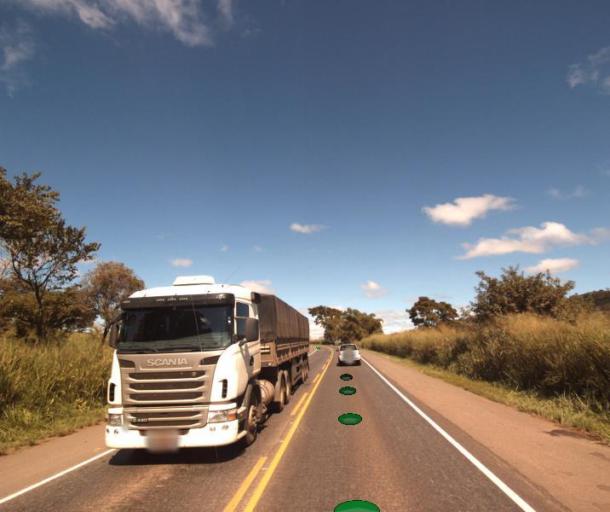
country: BR
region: Goias
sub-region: Rialma
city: Rialma
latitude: -15.2829
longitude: -49.5602
